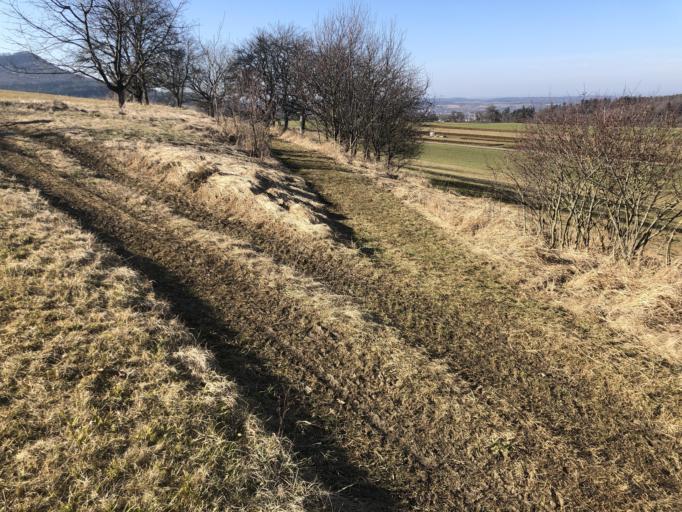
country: DE
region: Baden-Wuerttemberg
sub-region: Tuebingen Region
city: Nehren
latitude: 48.4101
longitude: 9.1034
